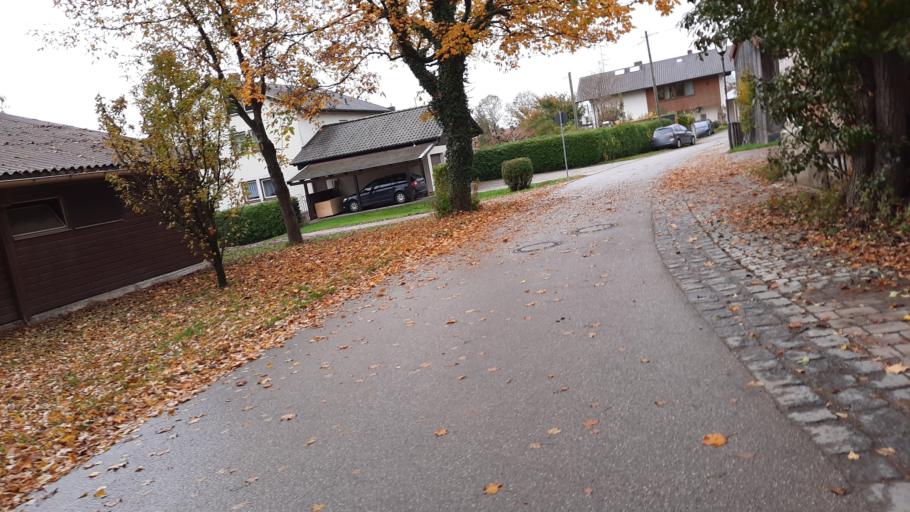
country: DE
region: Bavaria
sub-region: Upper Bavaria
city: Zorneding
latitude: 48.0817
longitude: 11.8279
